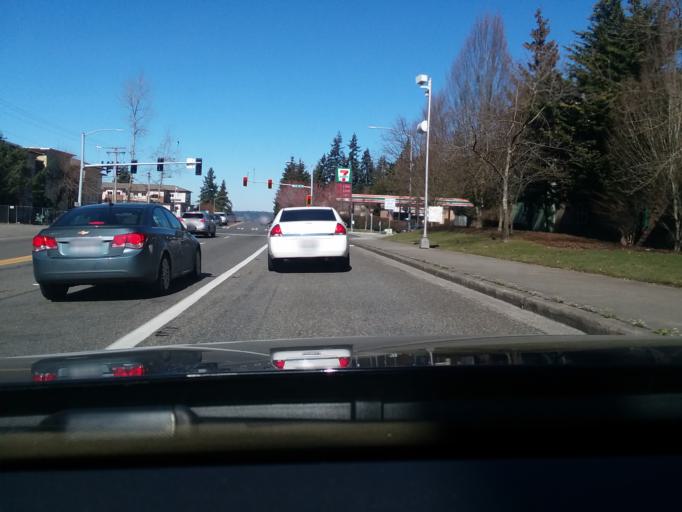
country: US
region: Washington
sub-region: Pierce County
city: Puyallup
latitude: 47.1615
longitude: -122.2929
